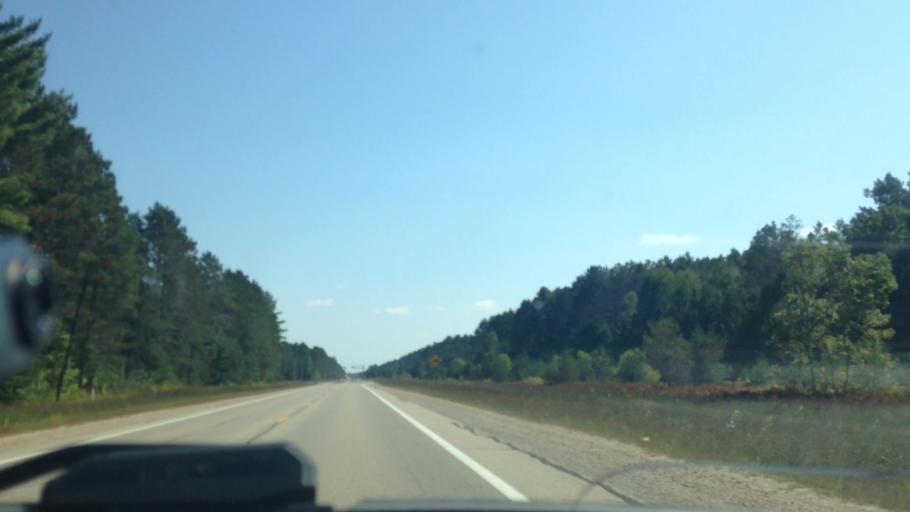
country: US
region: Michigan
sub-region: Alger County
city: Munising
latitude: 46.3693
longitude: -86.5396
